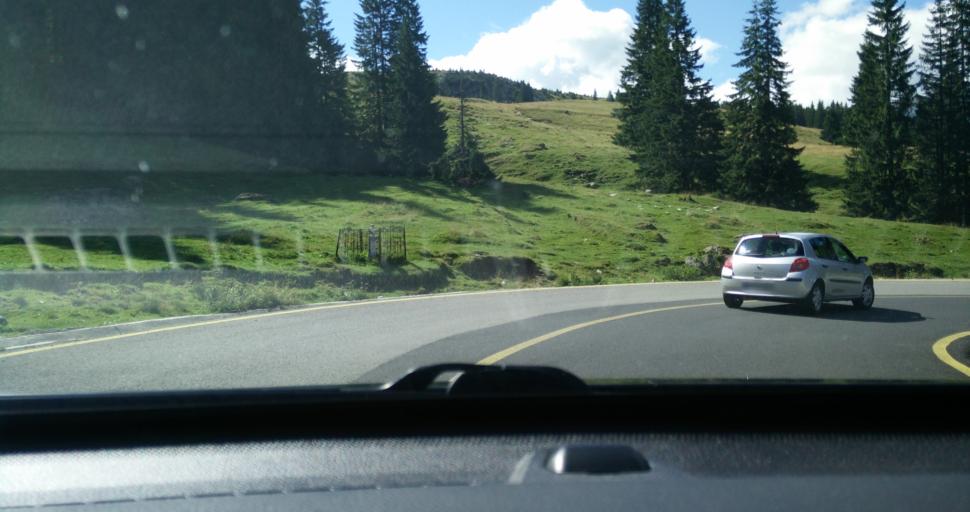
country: RO
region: Gorj
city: Novaci-Straini
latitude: 45.3902
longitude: 23.6370
